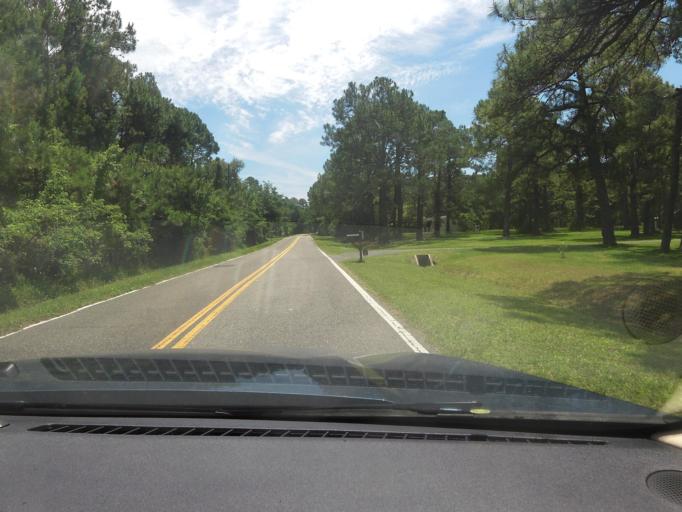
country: US
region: Florida
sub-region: Duval County
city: Atlantic Beach
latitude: 30.4546
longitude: -81.4668
